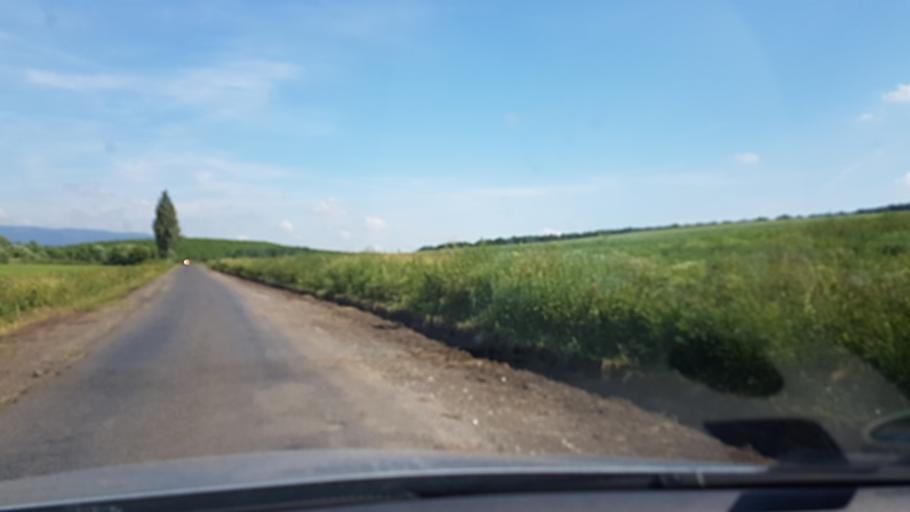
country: HU
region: Borsod-Abauj-Zemplen
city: Saly
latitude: 47.9365
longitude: 20.7105
